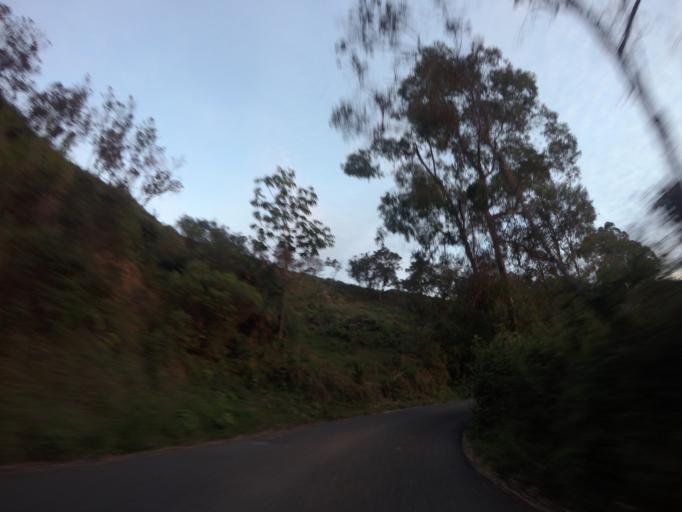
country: CO
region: Caldas
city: Manzanares
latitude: 5.2680
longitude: -75.1247
